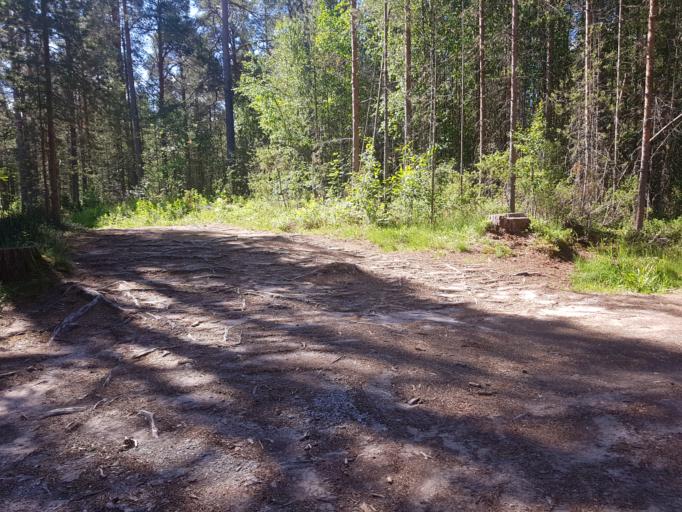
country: RU
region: Republic of Karelia
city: Yushkozero
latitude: 64.7433
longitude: 32.0980
